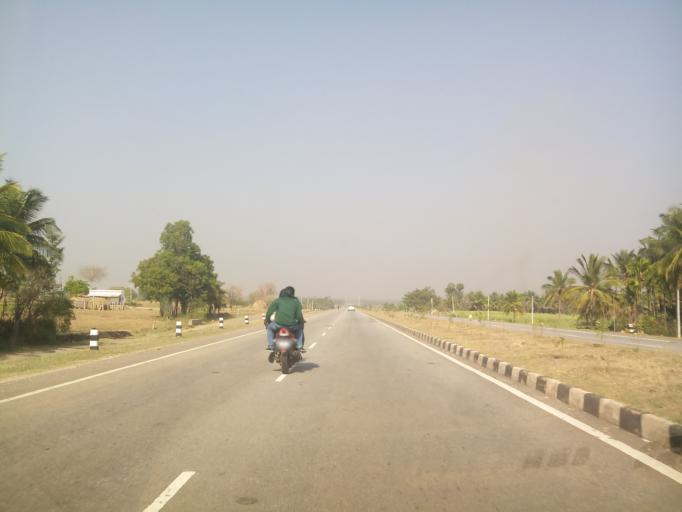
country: IN
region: Karnataka
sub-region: Tumkur
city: Kunigal
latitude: 13.0050
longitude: 77.0119
